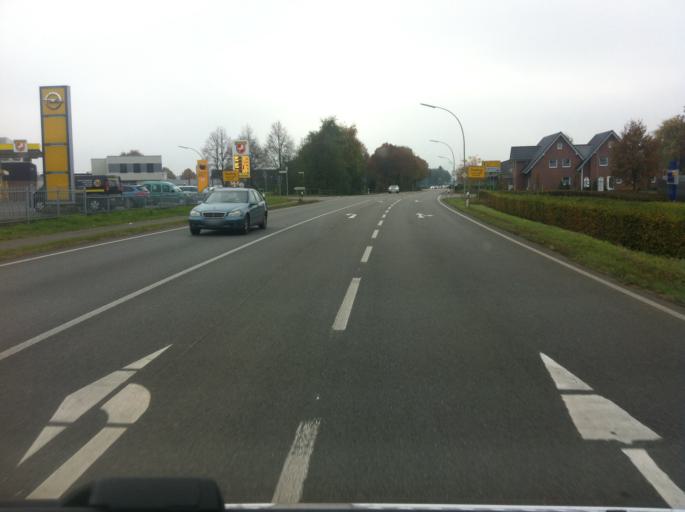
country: DE
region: North Rhine-Westphalia
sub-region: Regierungsbezirk Munster
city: Sudlohn
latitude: 51.9363
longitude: 6.8201
